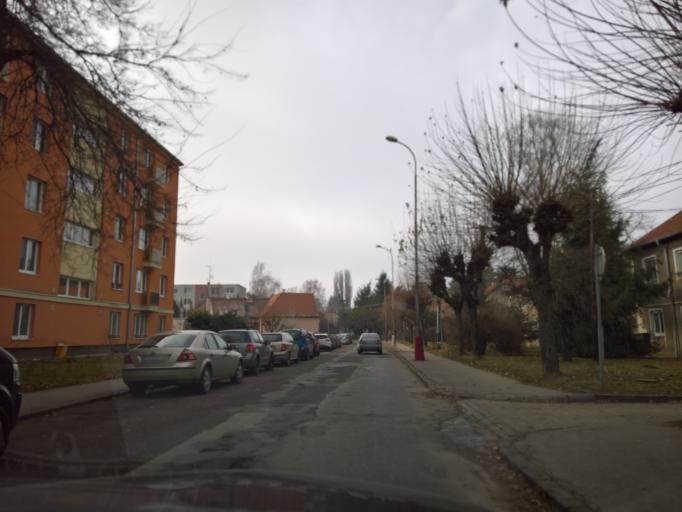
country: SK
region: Nitriansky
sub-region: Okres Nitra
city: Nitra
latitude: 48.3154
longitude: 18.0822
